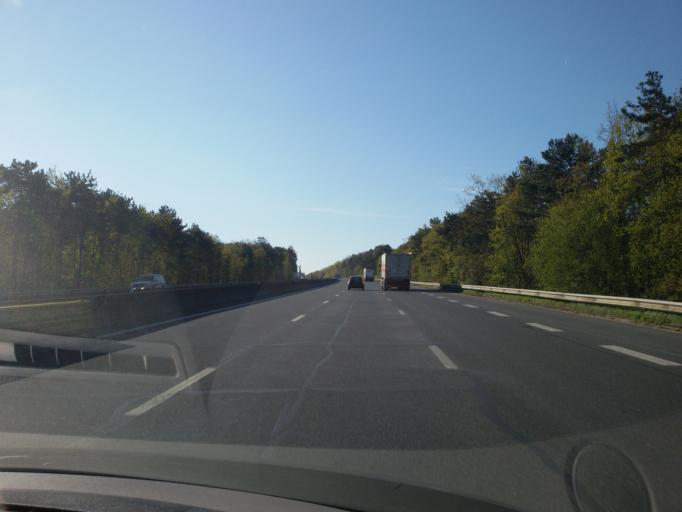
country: FR
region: Ile-de-France
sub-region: Departement de Seine-et-Marne
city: Bagneaux-sur-Loing
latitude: 48.2585
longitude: 2.7259
